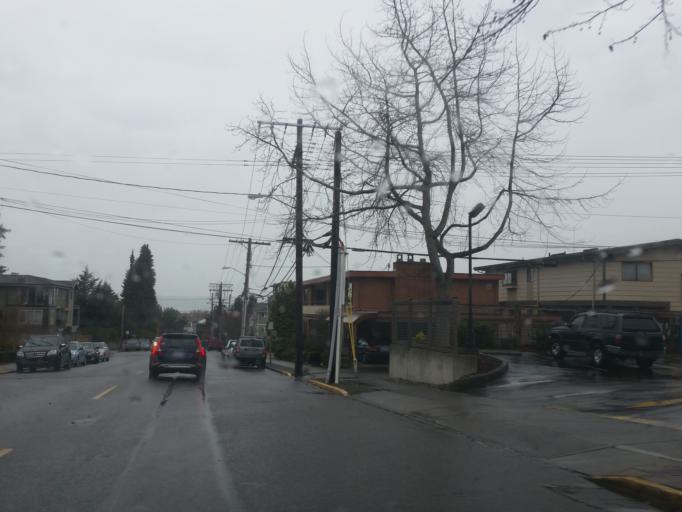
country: US
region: Washington
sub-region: Snohomish County
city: Edmonds
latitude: 47.8073
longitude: -122.3778
